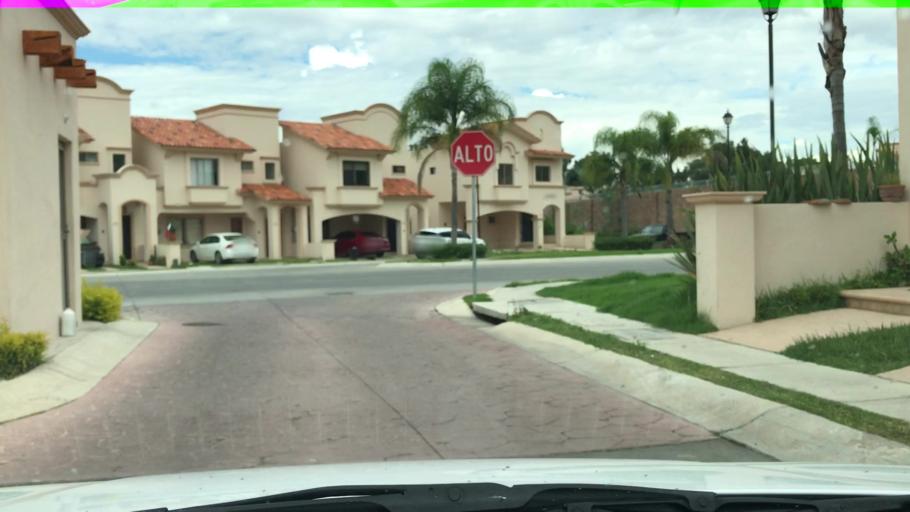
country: MX
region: Jalisco
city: Nicolas R Casillas
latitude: 20.5413
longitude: -103.4858
